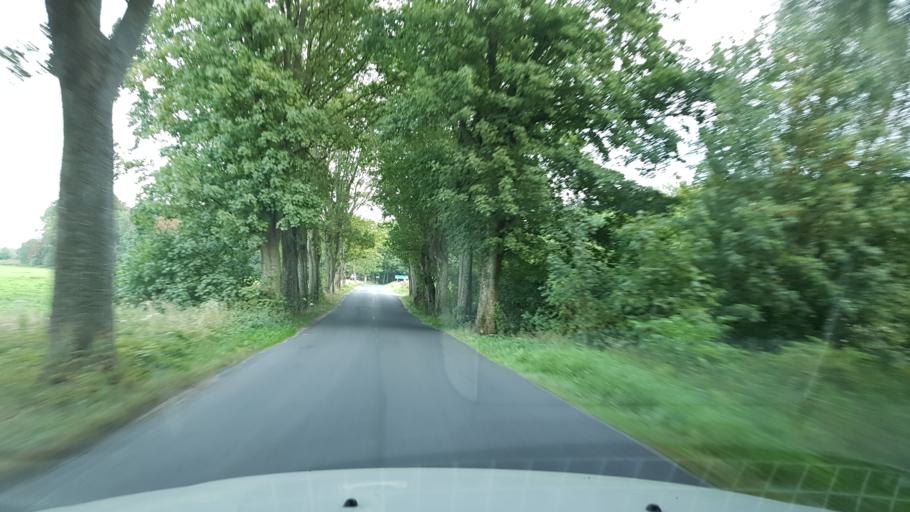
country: PL
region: West Pomeranian Voivodeship
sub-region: Powiat koszalinski
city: Mielno
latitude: 54.2293
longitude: 16.0208
